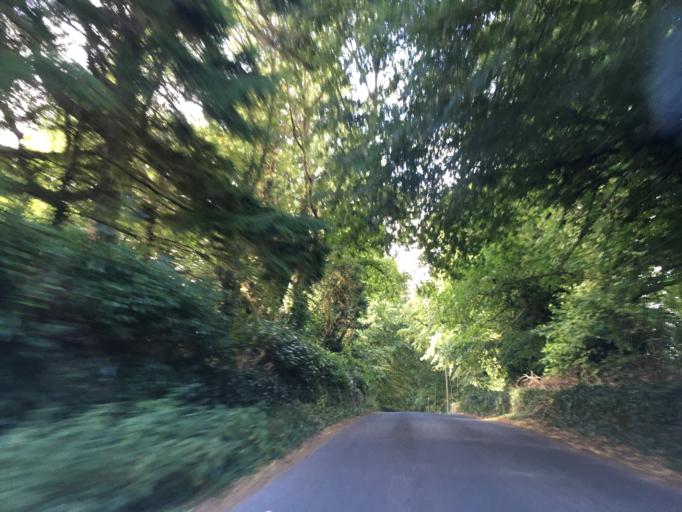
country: IE
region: Munster
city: Cahir
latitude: 52.2820
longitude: -7.9536
